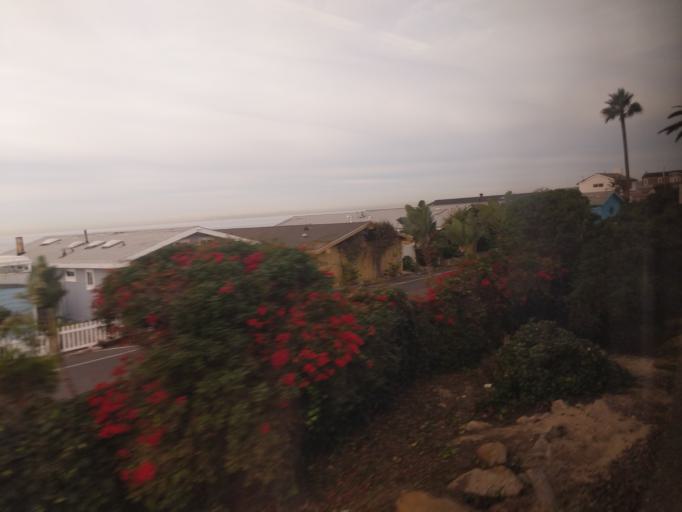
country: US
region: California
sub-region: Orange County
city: San Clemente
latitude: 33.4320
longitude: -117.6328
